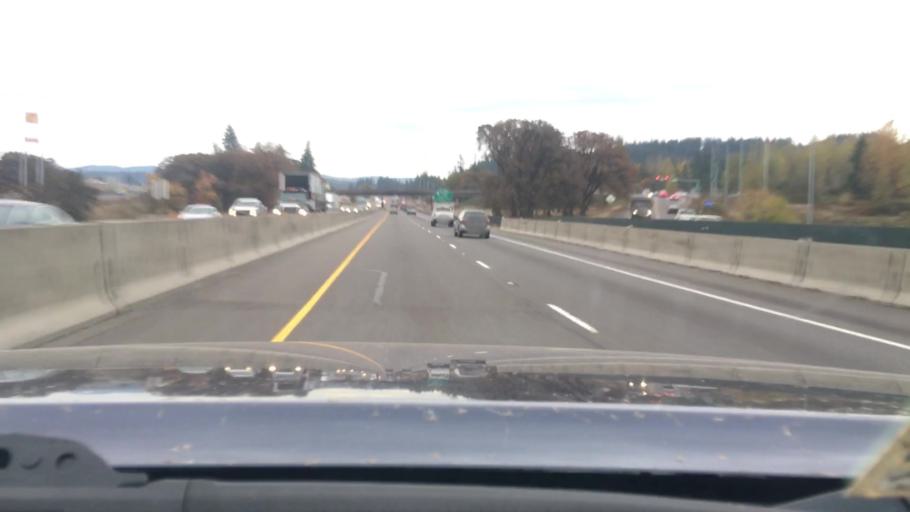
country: US
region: Oregon
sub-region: Lane County
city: Springfield
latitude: 44.0163
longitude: -123.0246
